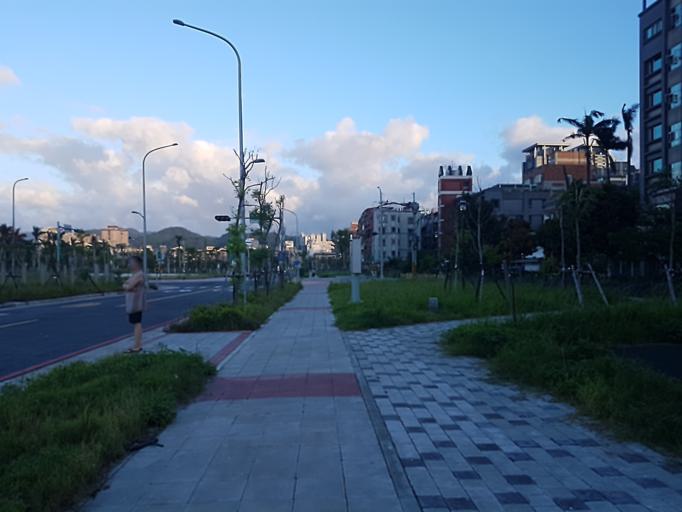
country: TW
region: Taipei
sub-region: Taipei
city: Banqiao
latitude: 24.9778
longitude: 121.5268
